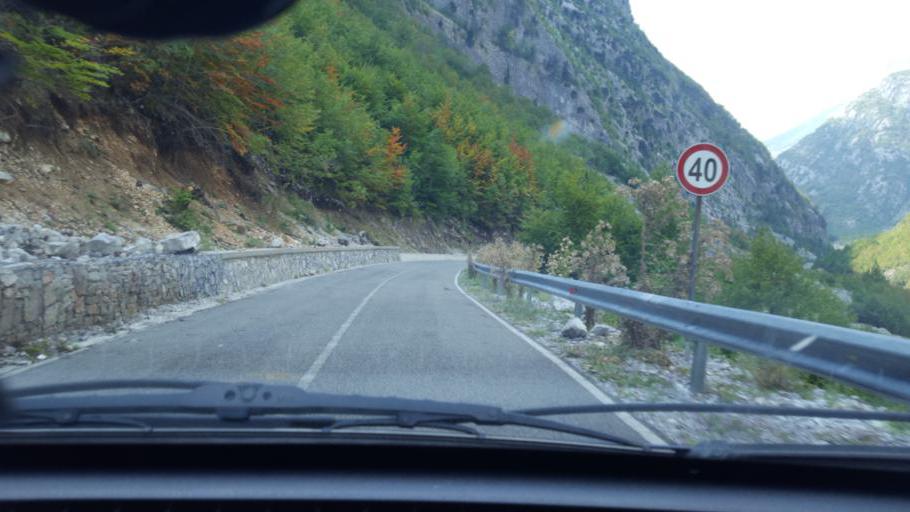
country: ME
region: Andrijevica
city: Andrijevica
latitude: 42.5331
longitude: 19.6599
